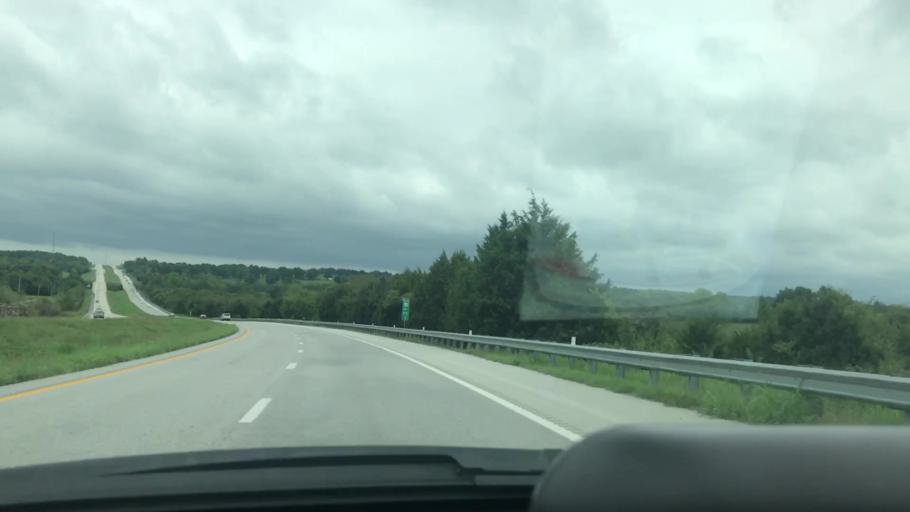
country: US
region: Missouri
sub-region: Greene County
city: Fair Grove
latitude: 37.4081
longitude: -93.1458
